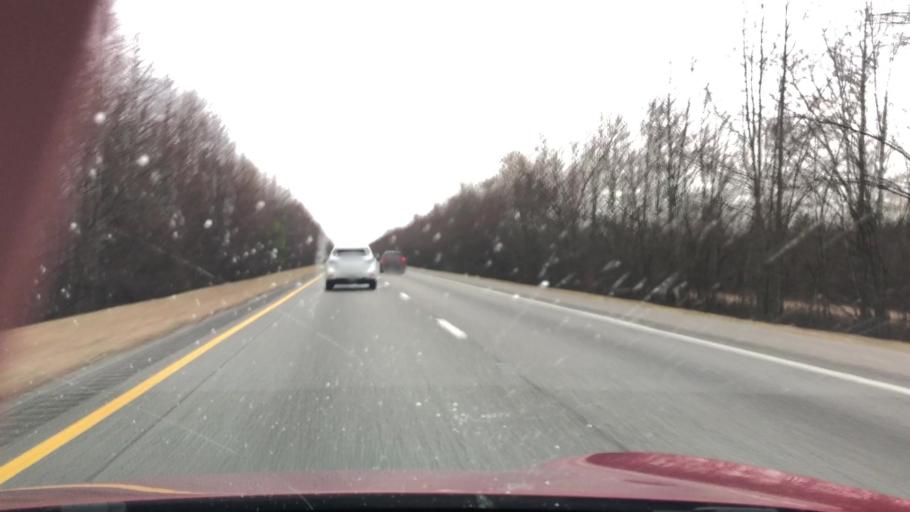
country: US
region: South Carolina
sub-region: Dillon County
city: Latta
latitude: 34.3240
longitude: -79.5784
